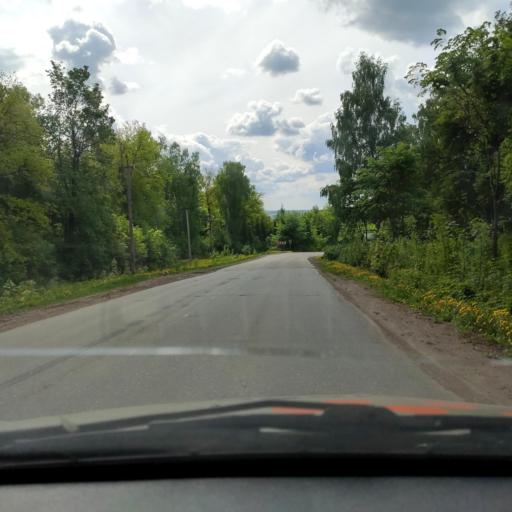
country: RU
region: Bashkortostan
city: Avdon
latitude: 54.6512
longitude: 55.7025
